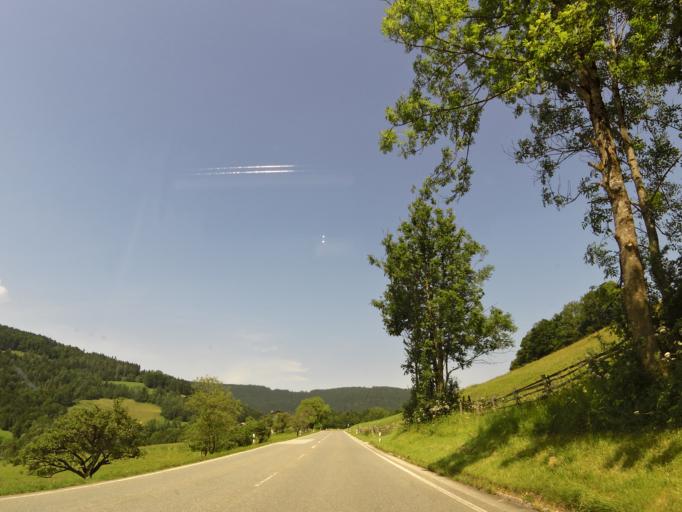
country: DE
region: Bavaria
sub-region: Upper Bavaria
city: Ruhpolding
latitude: 47.7502
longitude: 12.6764
